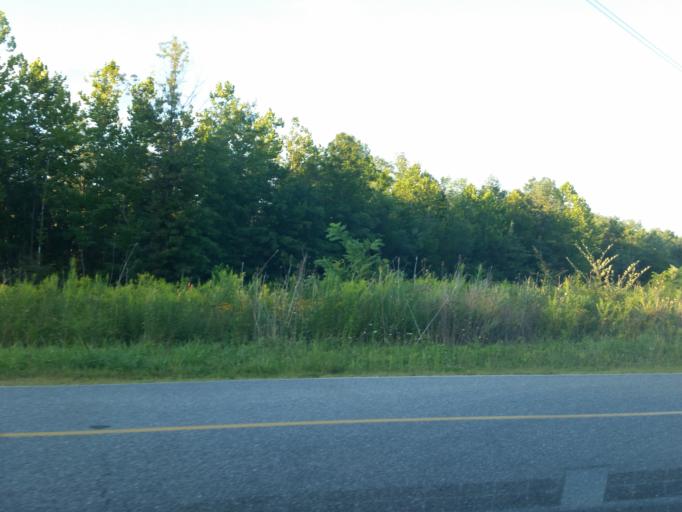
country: US
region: Pennsylvania
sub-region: Lebanon County
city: Jonestown
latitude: 40.4149
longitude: -76.5039
